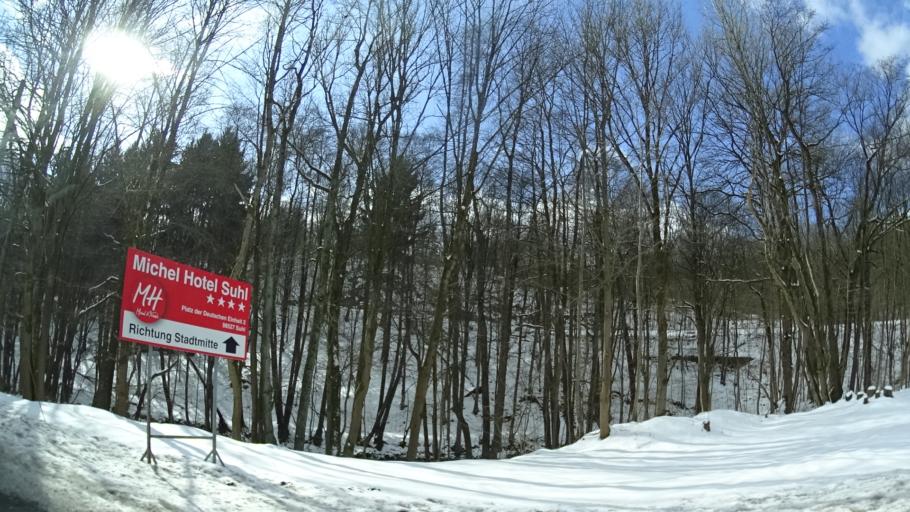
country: DE
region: Thuringia
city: Suhl
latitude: 50.6260
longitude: 10.6976
